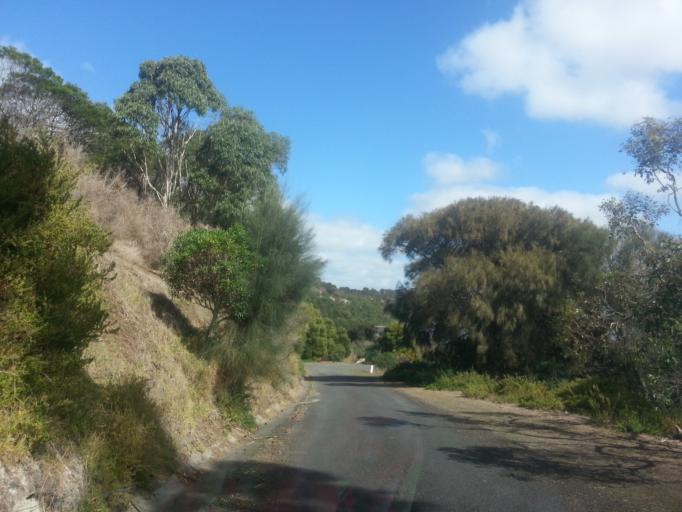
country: AU
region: Victoria
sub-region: Warrnambool
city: Warrnambool
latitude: -38.3271
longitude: 142.3667
